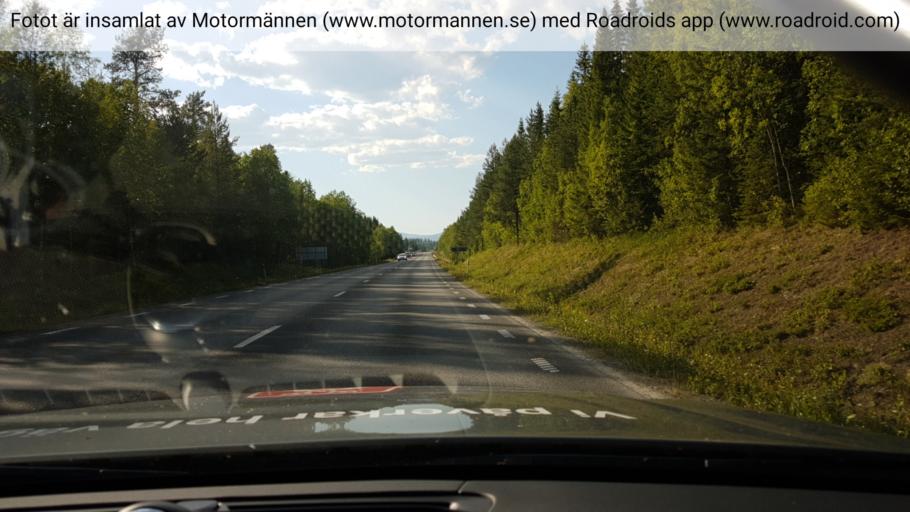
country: SE
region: Jaemtland
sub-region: Are Kommun
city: Are
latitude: 63.3217
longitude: 13.2399
